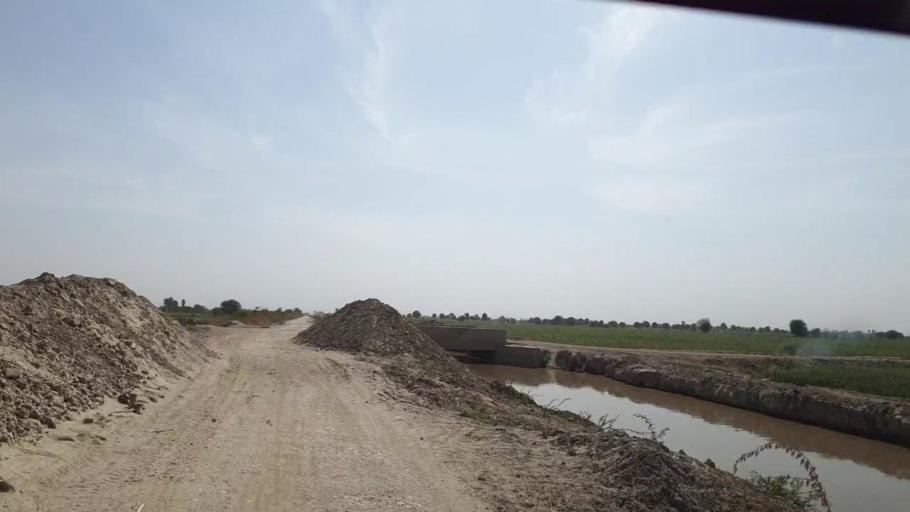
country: PK
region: Sindh
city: Nabisar
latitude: 25.0963
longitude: 69.5819
